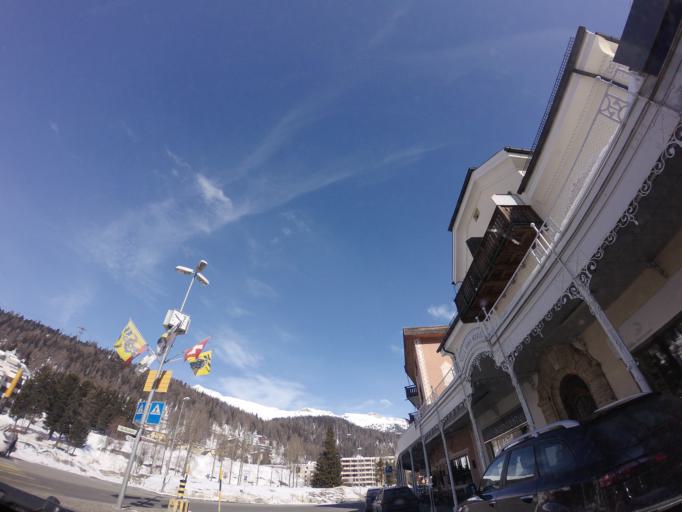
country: CH
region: Grisons
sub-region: Maloja District
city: Saint Moritz
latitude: 46.4867
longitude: 9.8364
